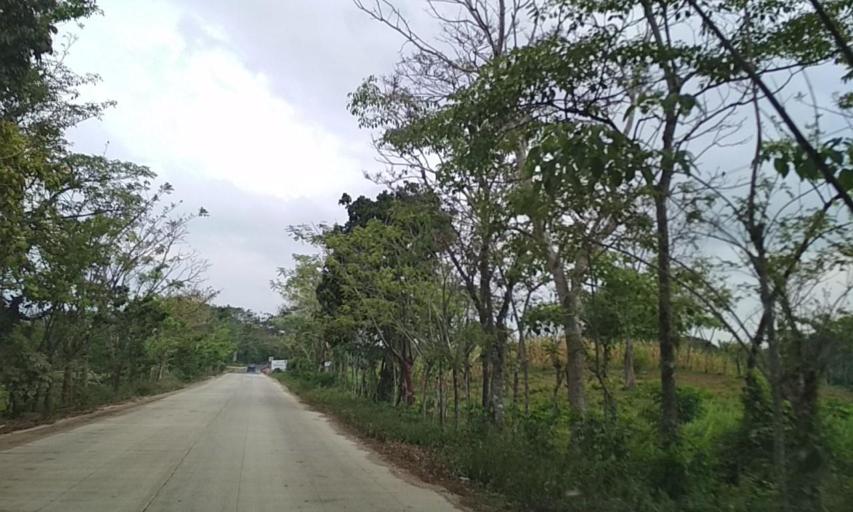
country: MX
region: Tabasco
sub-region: Huimanguillo
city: Francisco Rueda
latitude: 17.6779
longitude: -94.0920
